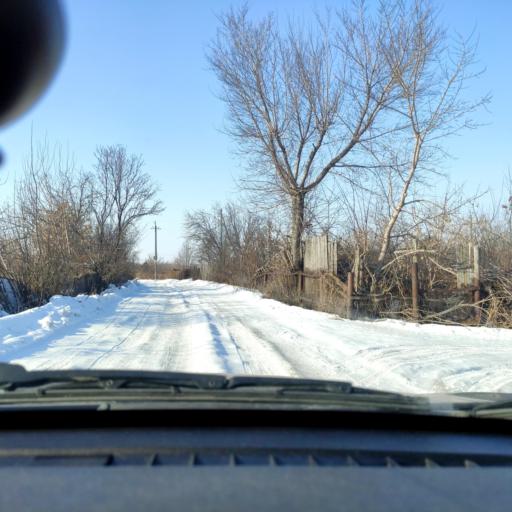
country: RU
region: Samara
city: Tol'yatti
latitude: 53.5710
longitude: 49.4528
